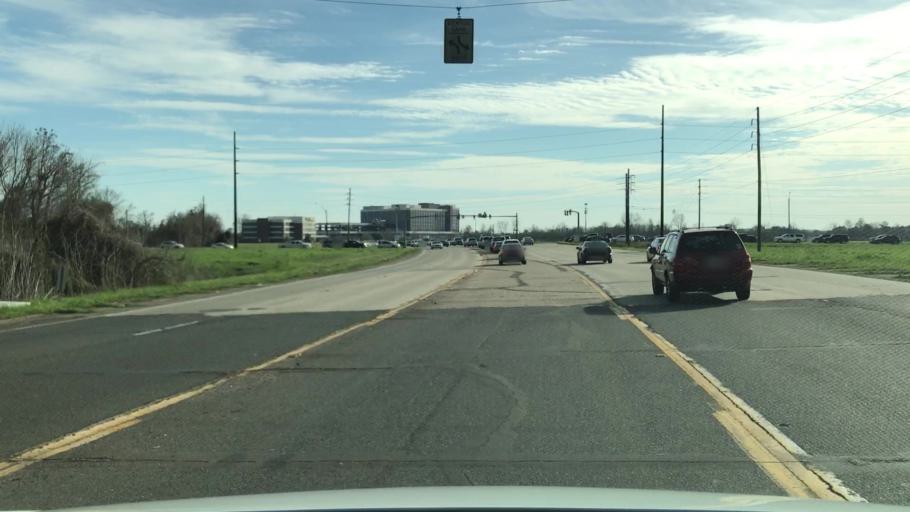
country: US
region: Louisiana
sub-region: Bossier Parish
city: Bossier City
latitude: 32.4402
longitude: -93.7060
